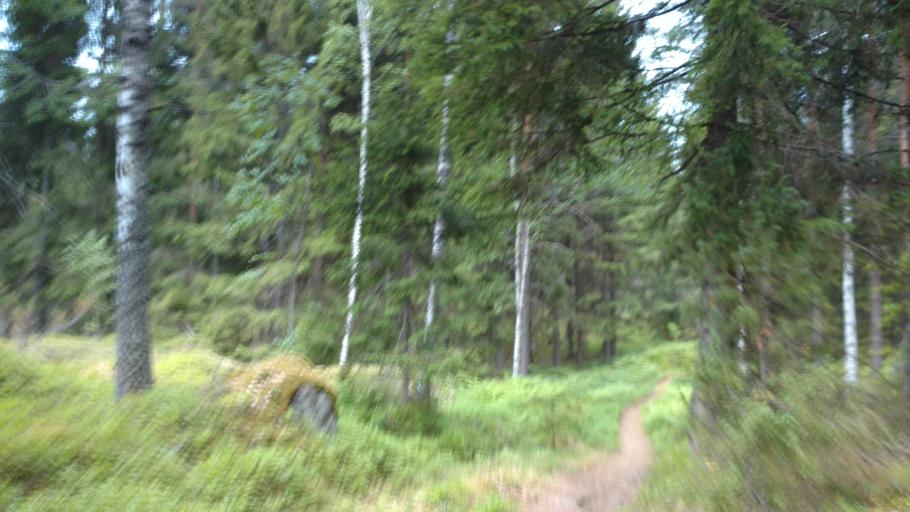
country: FI
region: Uusimaa
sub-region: Raaseporin
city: Pohja
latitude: 60.1174
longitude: 23.5675
